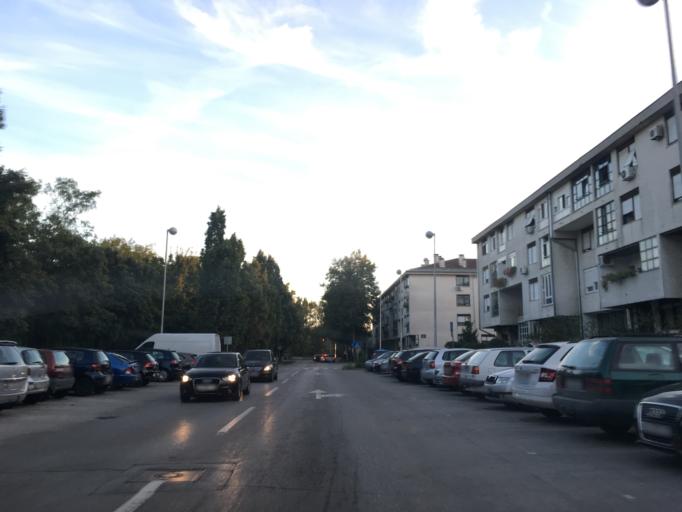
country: HR
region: Grad Zagreb
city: Jankomir
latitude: 45.7857
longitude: 15.9412
